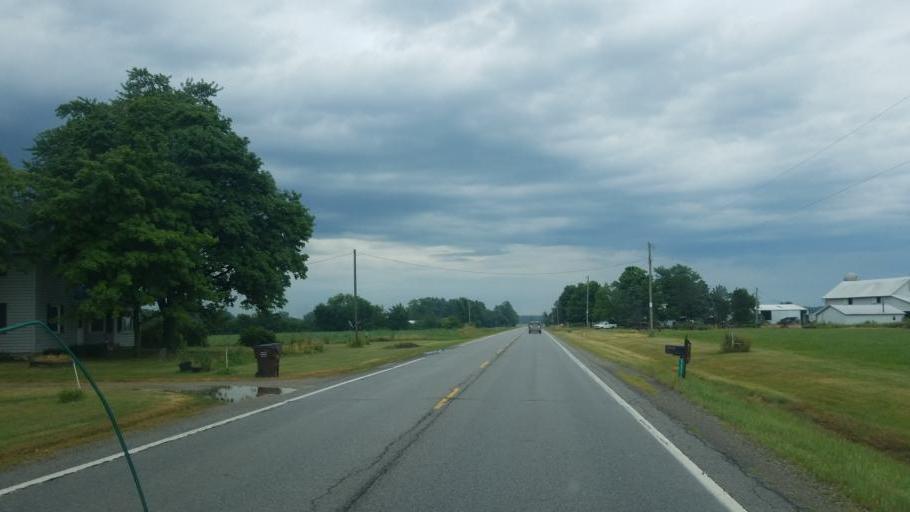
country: US
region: Ohio
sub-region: Williams County
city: Edgerton
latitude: 41.4462
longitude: -84.6802
